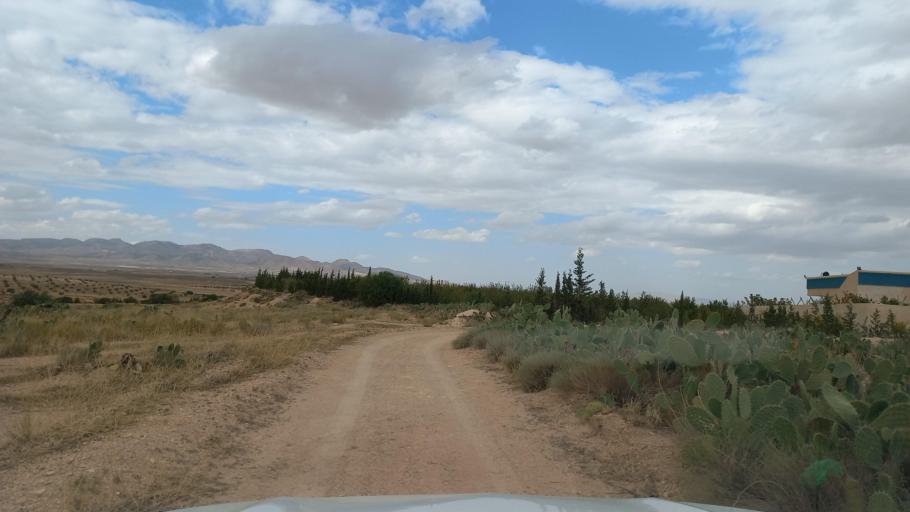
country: TN
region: Al Qasrayn
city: Sbiba
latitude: 35.3792
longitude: 9.1289
